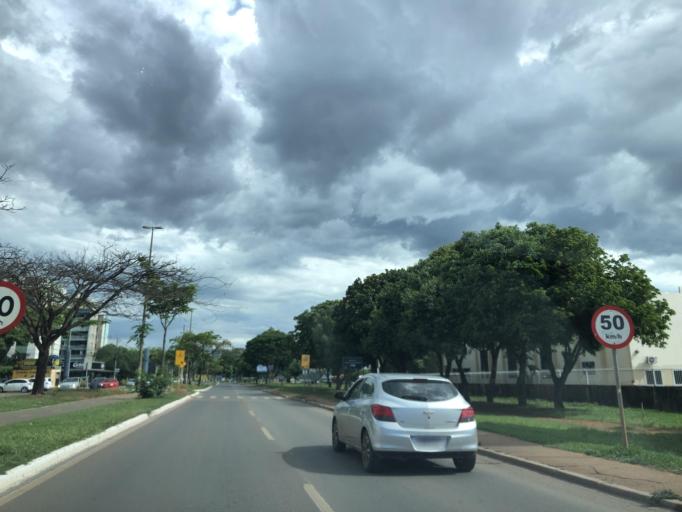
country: BR
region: Goias
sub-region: Luziania
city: Luziania
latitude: -16.0134
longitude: -48.0680
